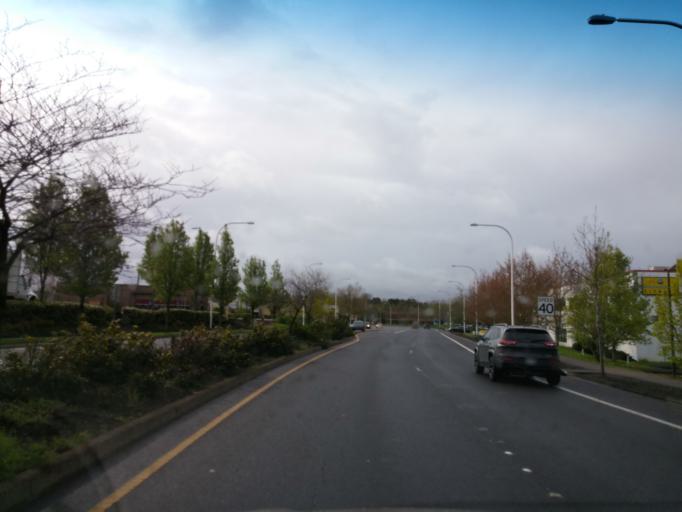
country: US
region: Oregon
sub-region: Washington County
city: Oak Hills
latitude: 45.5320
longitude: -122.8455
